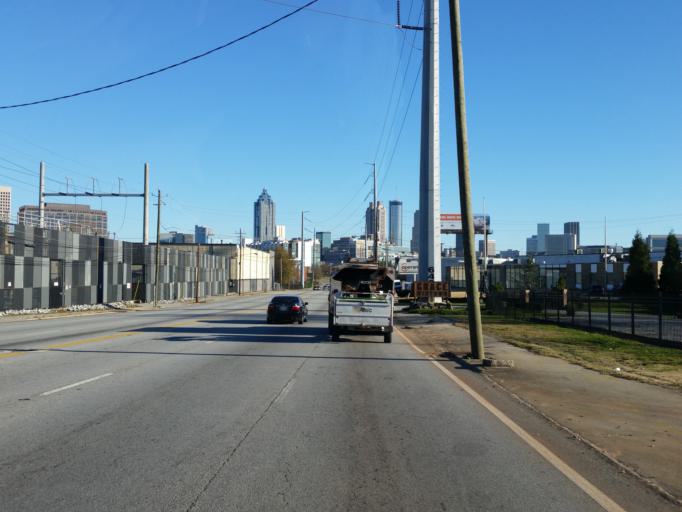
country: US
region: Georgia
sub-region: Fulton County
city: Atlanta
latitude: 33.7724
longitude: -84.4081
